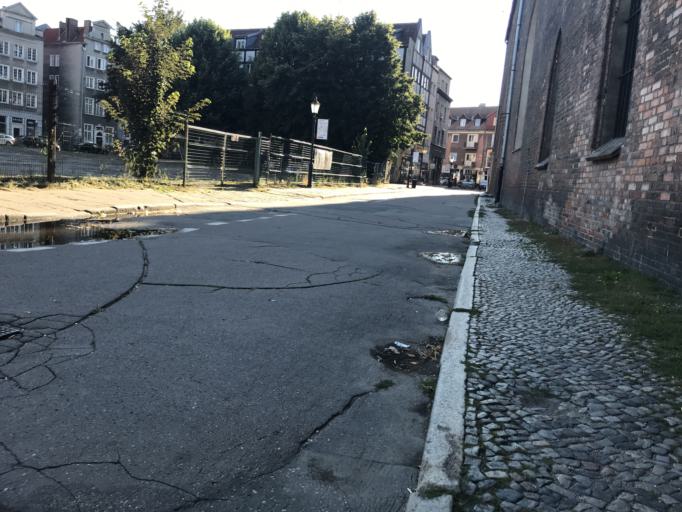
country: PL
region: Pomeranian Voivodeship
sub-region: Gdansk
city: Gdansk
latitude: 54.3521
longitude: 18.6526
